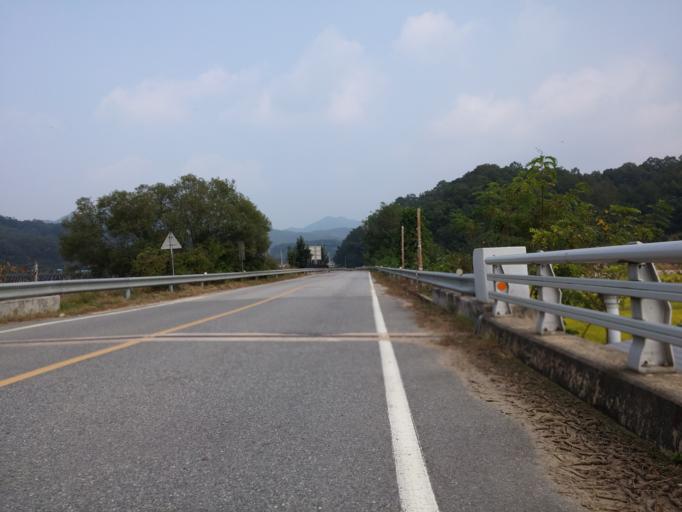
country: KR
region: Chungcheongbuk-do
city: Yong-dong
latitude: 36.3498
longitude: 127.8161
